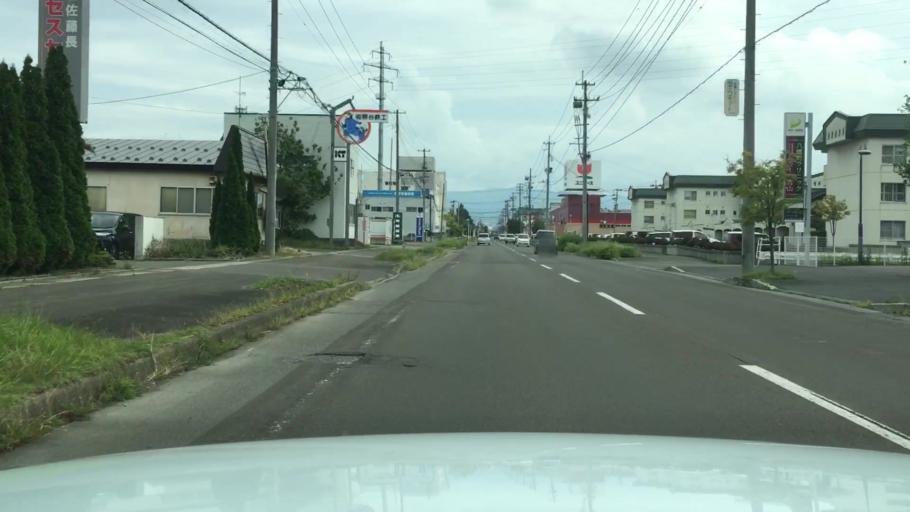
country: JP
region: Aomori
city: Hirosaki
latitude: 40.6242
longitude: 140.4852
